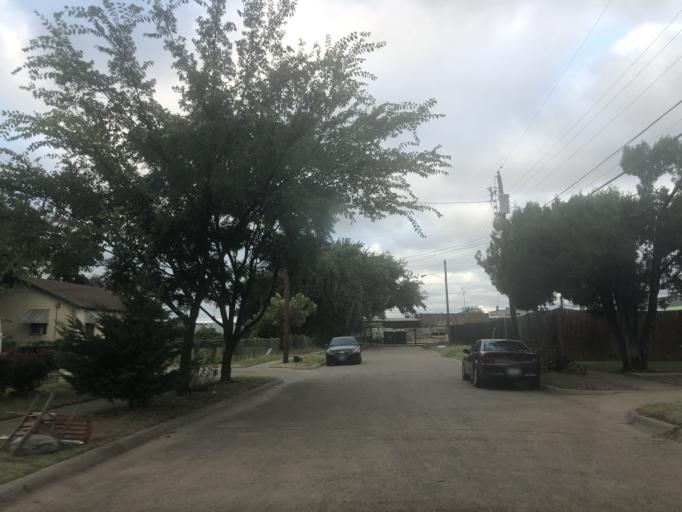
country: US
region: Texas
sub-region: Dallas County
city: University Park
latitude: 32.8301
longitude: -96.8561
